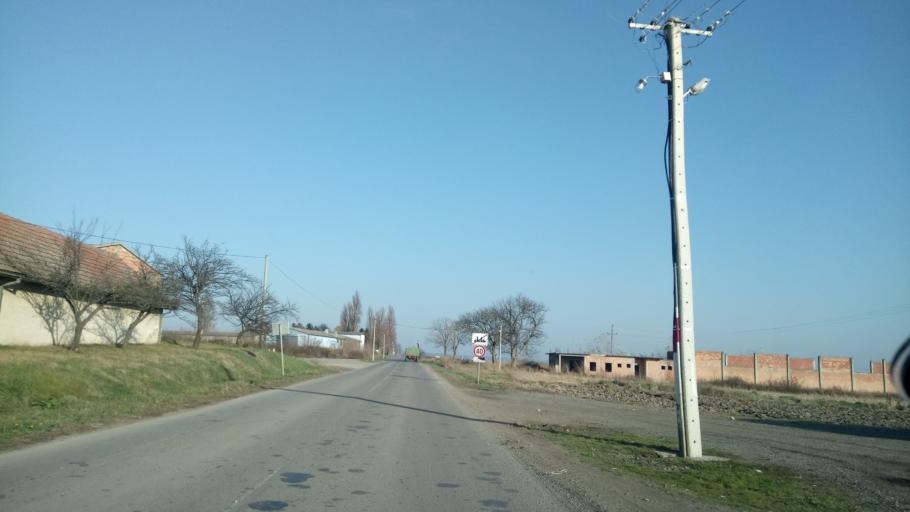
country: RS
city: Beska
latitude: 45.1312
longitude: 20.0812
